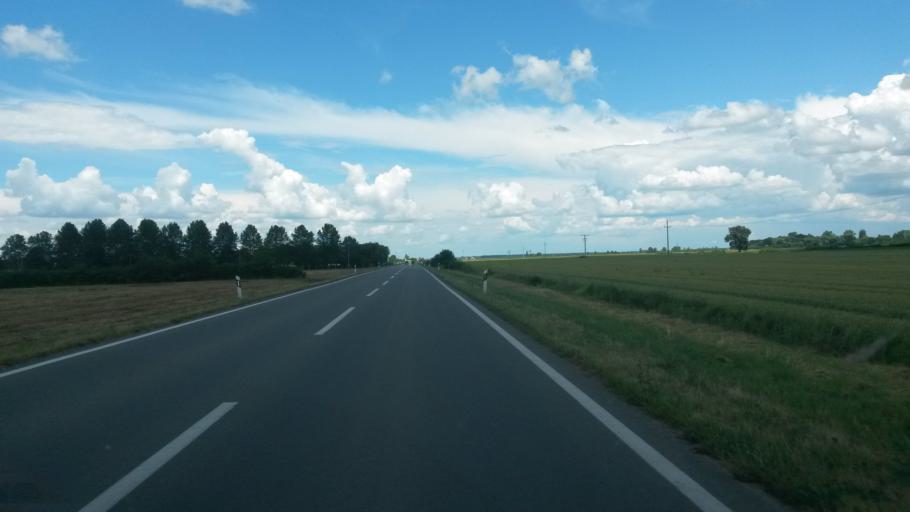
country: HR
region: Osjecko-Baranjska
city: Vuka
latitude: 45.4643
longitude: 18.5214
